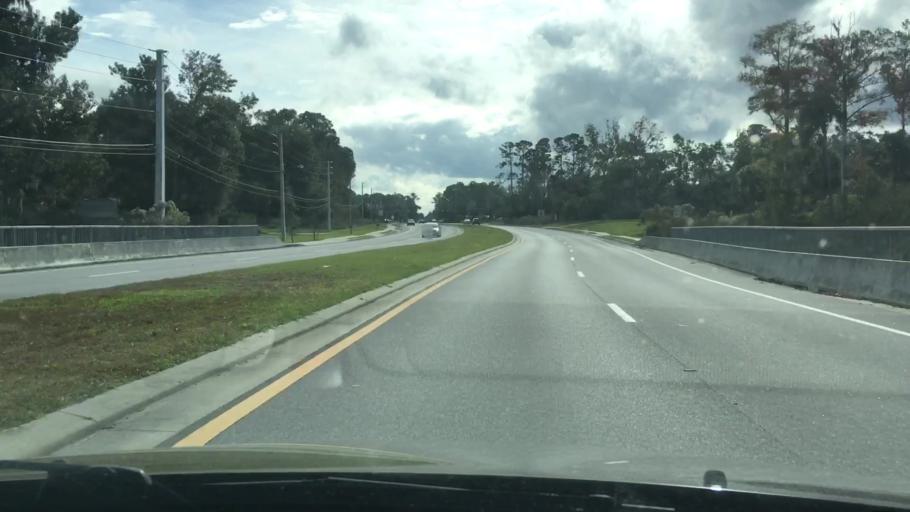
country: US
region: Florida
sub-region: Volusia County
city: Ormond Beach
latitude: 29.2571
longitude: -81.1291
